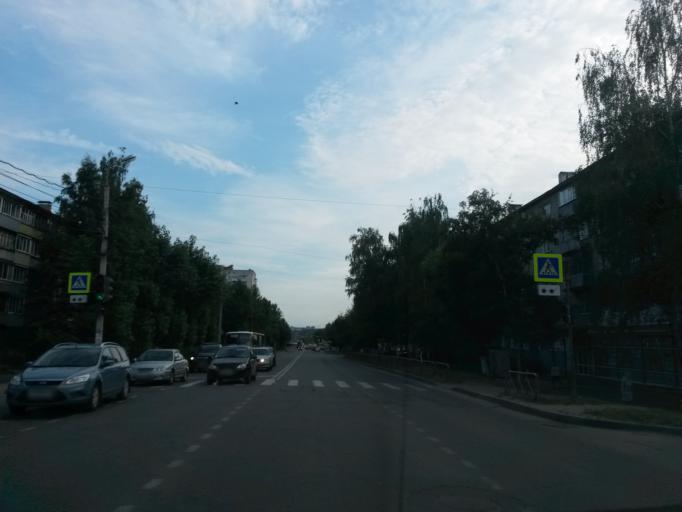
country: RU
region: Jaroslavl
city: Yaroslavl
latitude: 57.6236
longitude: 39.8485
